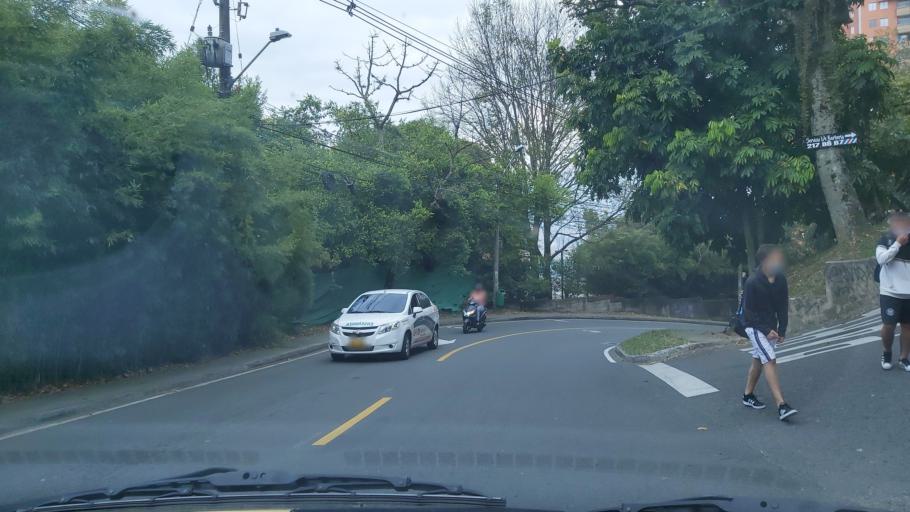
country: CO
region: Antioquia
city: Medellin
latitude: 6.2269
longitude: -75.5621
